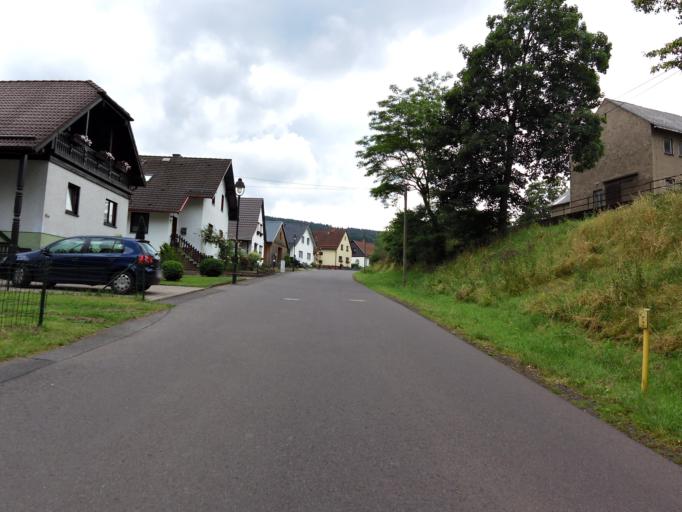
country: DE
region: Thuringia
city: Tabarz
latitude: 50.8877
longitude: 10.4829
